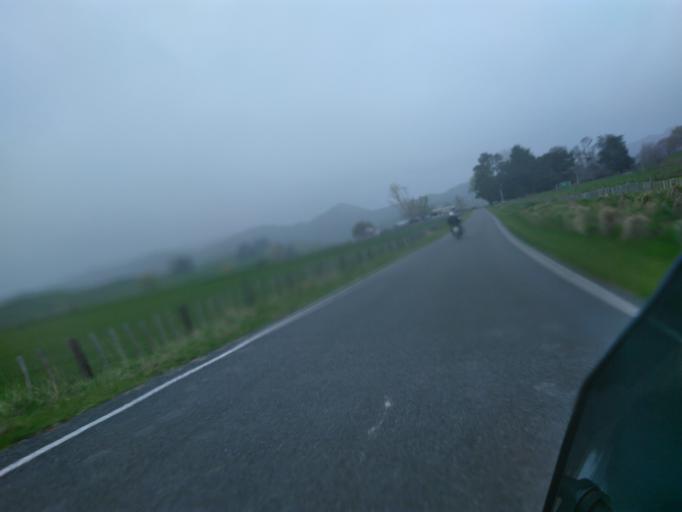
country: NZ
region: Gisborne
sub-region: Gisborne District
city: Gisborne
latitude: -38.6500
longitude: 177.7259
